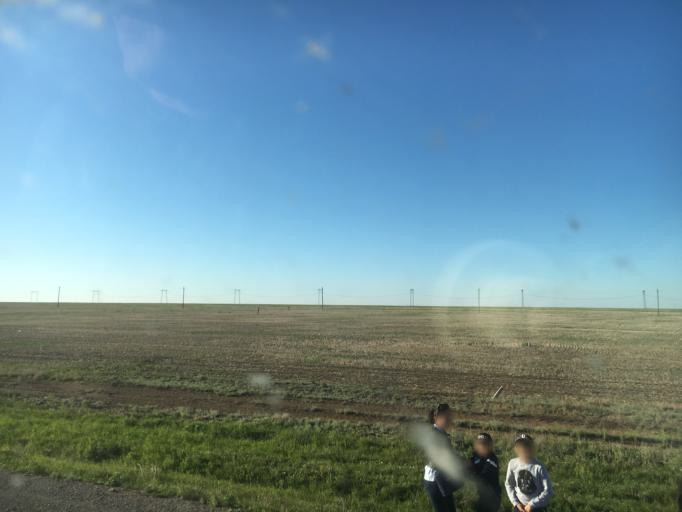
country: KZ
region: Aqtoebe
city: Batamshinskiy
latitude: 50.2483
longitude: 57.9885
